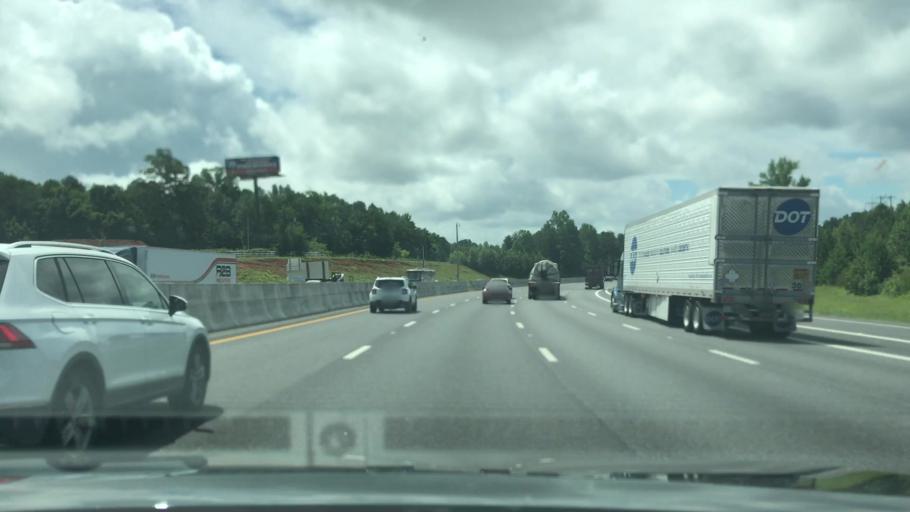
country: US
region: South Carolina
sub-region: York County
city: Lesslie
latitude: 34.9372
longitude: -80.9713
